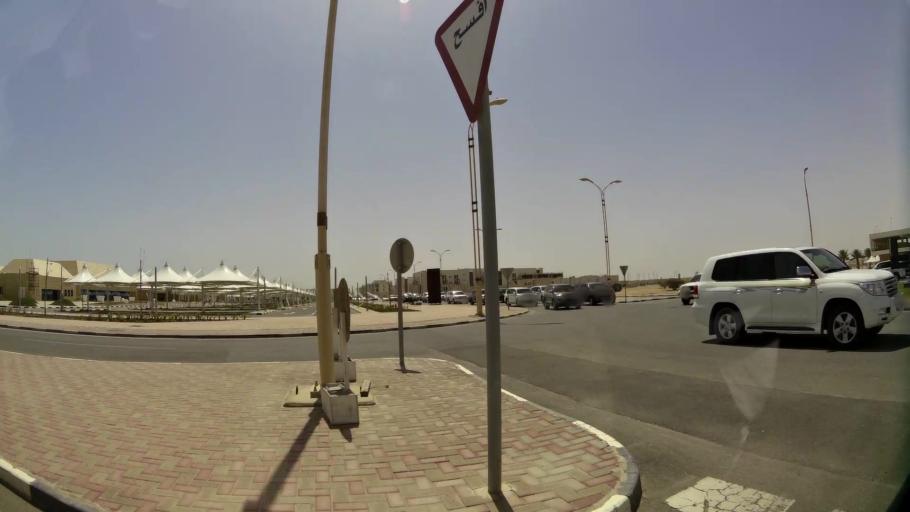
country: QA
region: Baladiyat Umm Salal
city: Umm Salal Muhammad
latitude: 25.3743
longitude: 51.4830
